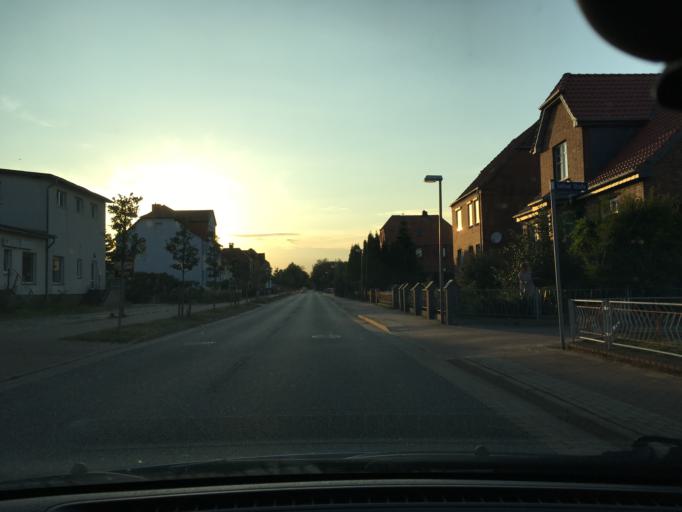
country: DE
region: Mecklenburg-Vorpommern
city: Boizenburg
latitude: 53.3787
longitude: 10.7565
